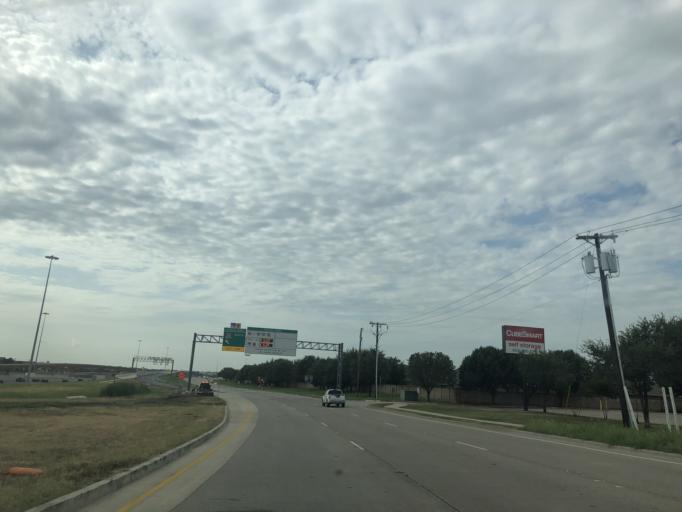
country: US
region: Texas
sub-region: Tarrant County
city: Blue Mound
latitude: 32.8713
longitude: -97.3180
